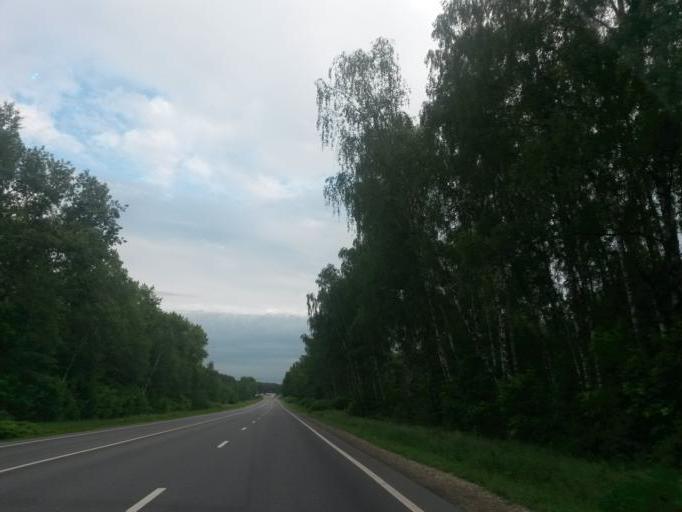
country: RU
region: Moskovskaya
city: Barybino
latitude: 55.2405
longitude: 37.8561
